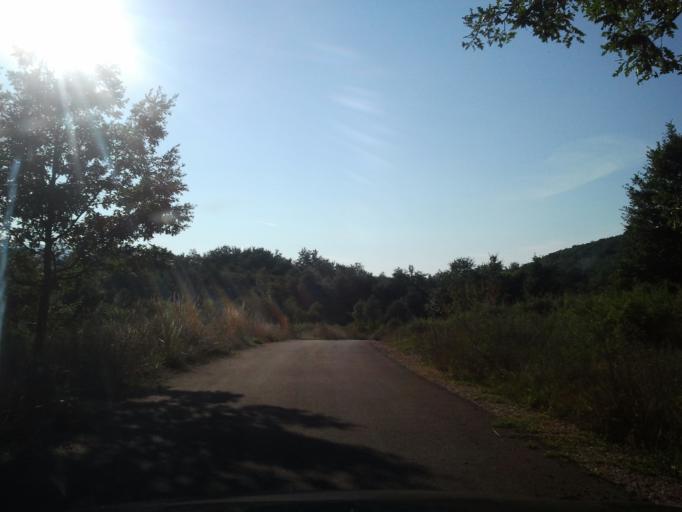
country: HR
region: Zadarska
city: Gracac
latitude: 44.3629
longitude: 15.7050
